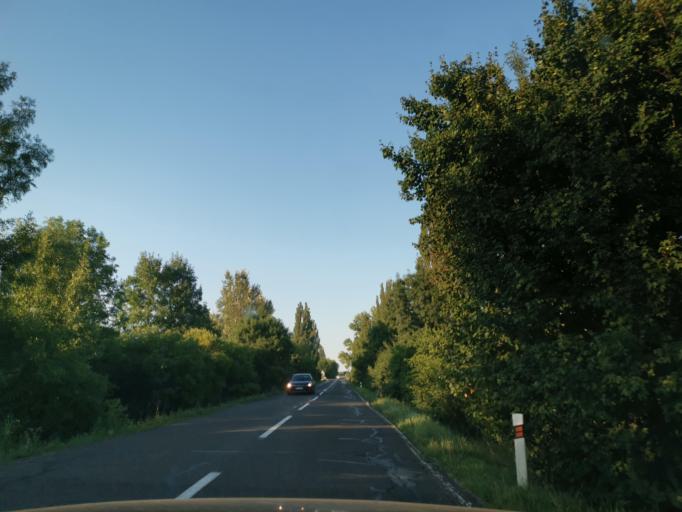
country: AT
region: Lower Austria
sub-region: Politischer Bezirk Mistelbach
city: Rabensburg
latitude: 48.6329
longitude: 16.9926
